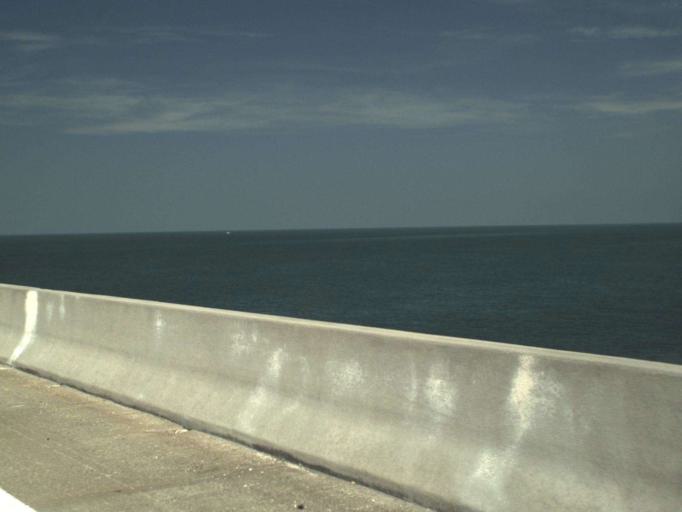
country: US
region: Florida
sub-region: Monroe County
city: Marathon
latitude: 24.7979
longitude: -80.8655
